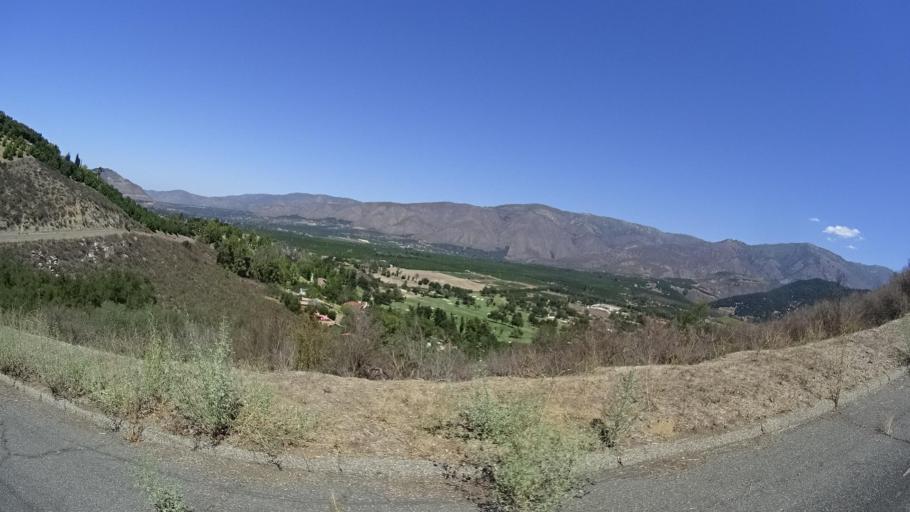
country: US
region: California
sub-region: San Diego County
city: Valley Center
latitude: 33.2975
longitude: -116.9902
